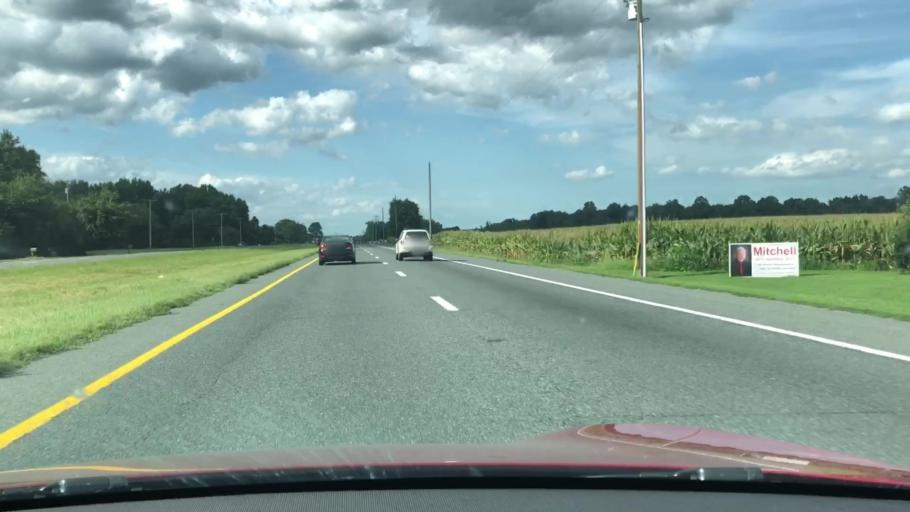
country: US
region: Delaware
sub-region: Sussex County
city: Bridgeville
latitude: 38.7730
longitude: -75.5922
